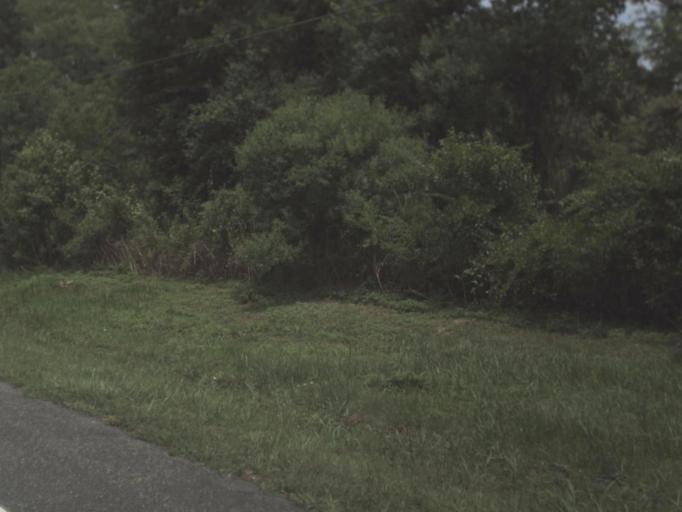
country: US
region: Florida
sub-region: Madison County
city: Madison
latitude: 30.4532
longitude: -83.4180
